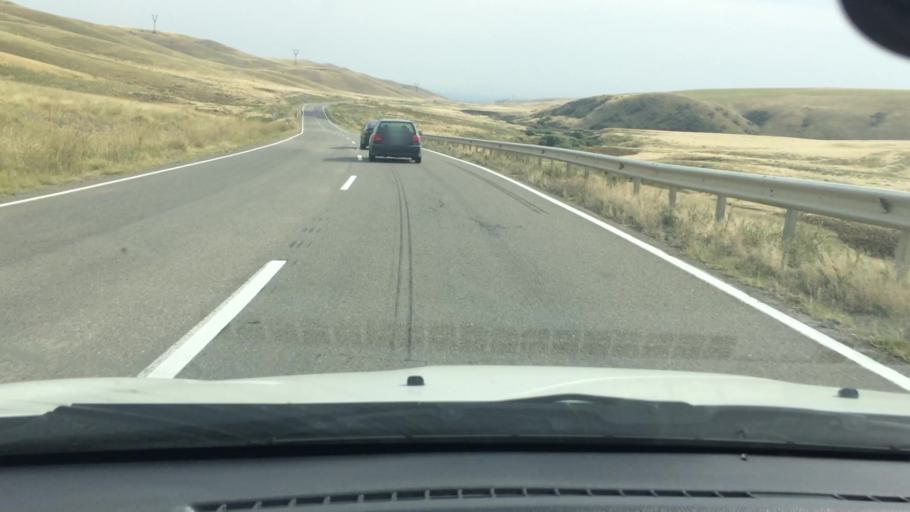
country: GE
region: Kvemo Kartli
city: Rust'avi
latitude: 41.5218
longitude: 44.9380
